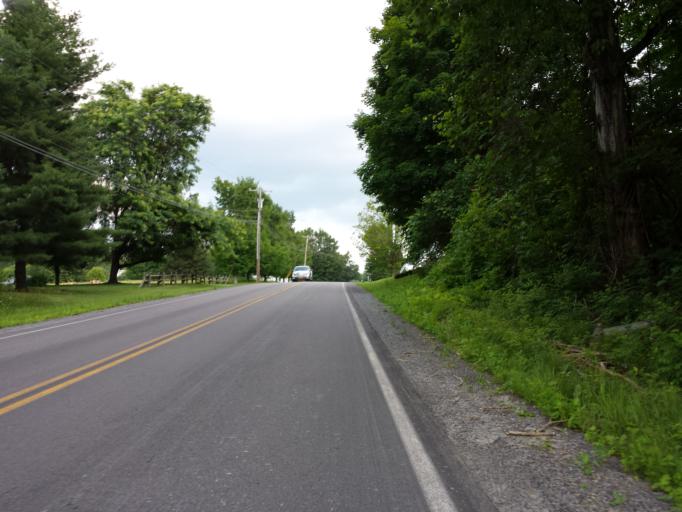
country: US
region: New York
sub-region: St. Lawrence County
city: Potsdam
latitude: 44.7188
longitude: -74.9094
